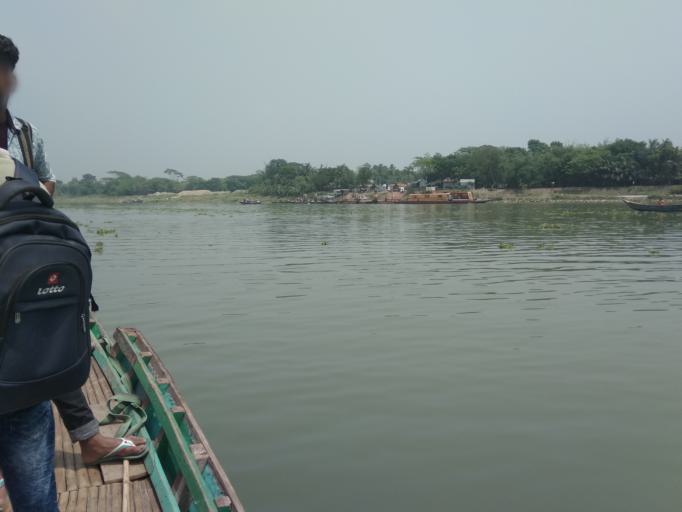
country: BD
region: Khulna
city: Kalia
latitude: 23.1949
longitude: 89.6915
